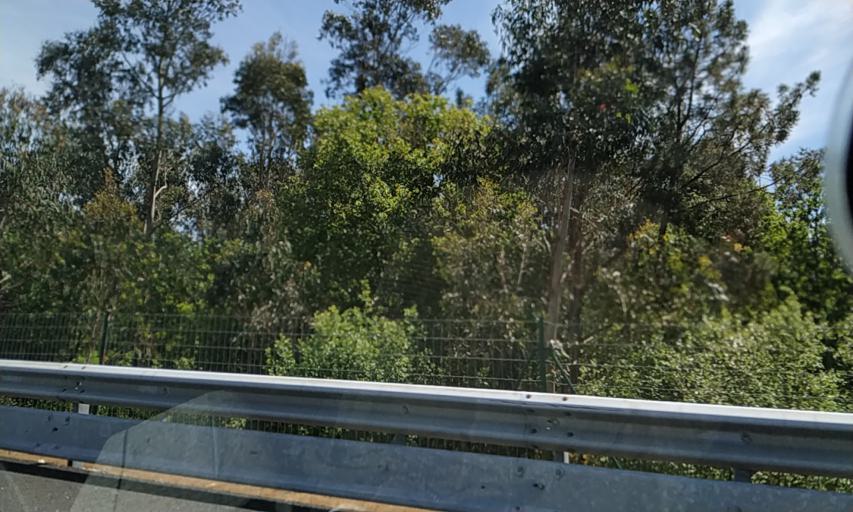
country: ES
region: Galicia
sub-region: Provincia da Coruna
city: Santiago de Compostela
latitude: 42.8120
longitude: -8.5798
